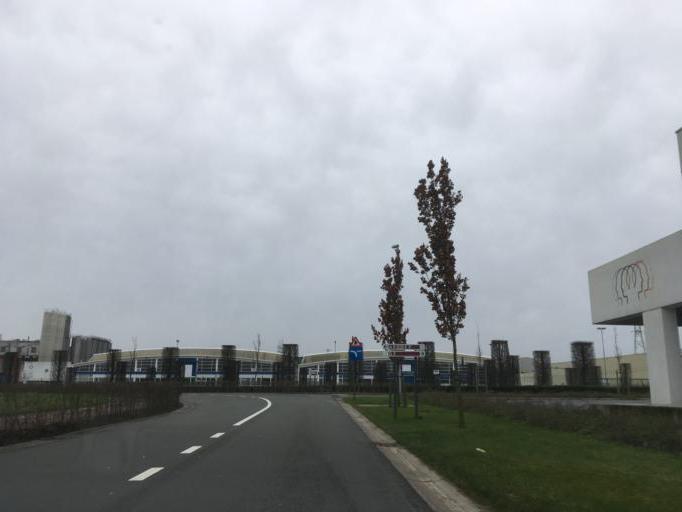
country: BE
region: Flanders
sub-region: Provincie West-Vlaanderen
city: Roeselare
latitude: 50.9716
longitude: 3.1257
